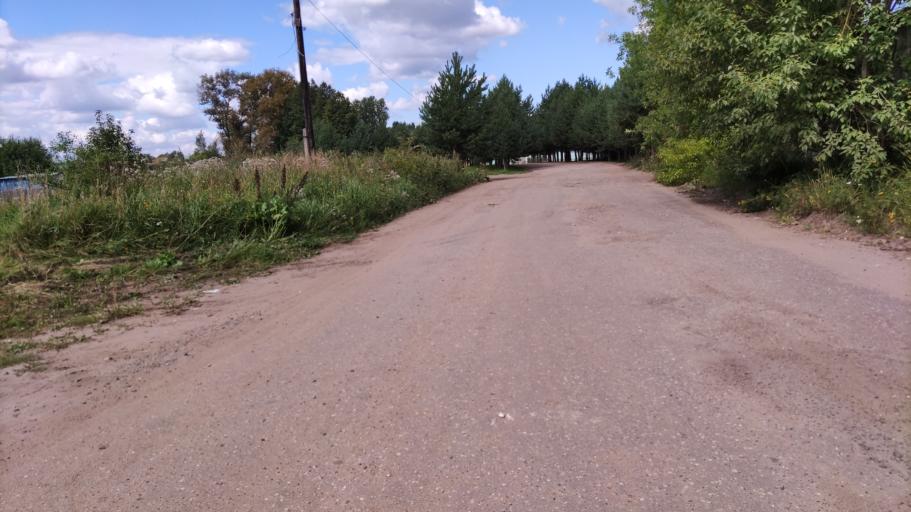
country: RU
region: Tverskaya
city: Rzhev
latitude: 56.2360
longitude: 34.3320
